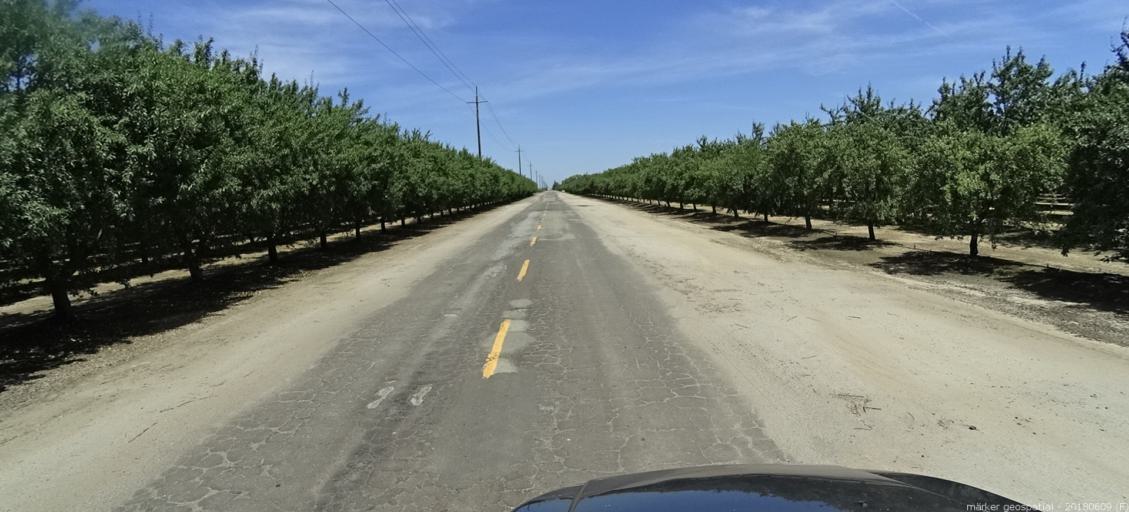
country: US
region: California
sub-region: Madera County
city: Parkwood
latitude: 36.9165
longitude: -120.0912
